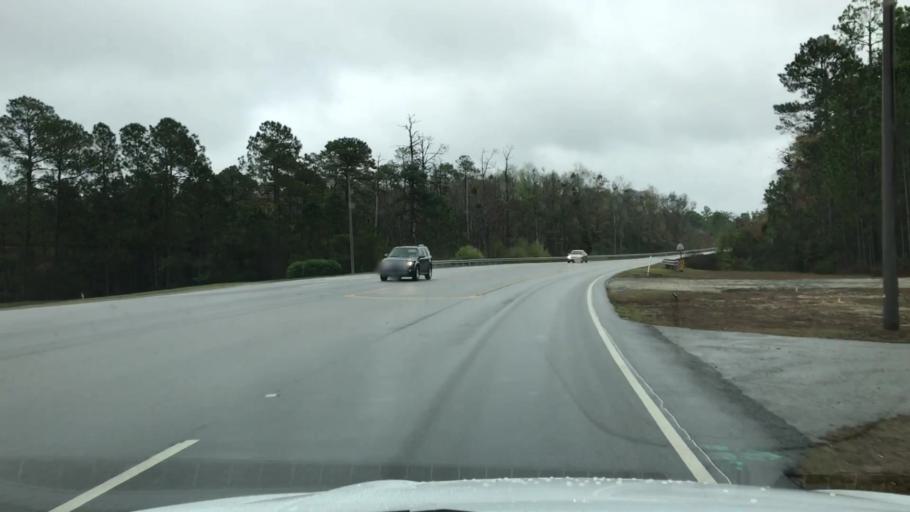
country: US
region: South Carolina
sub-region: Horry County
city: Forestbrook
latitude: 33.7595
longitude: -78.9187
